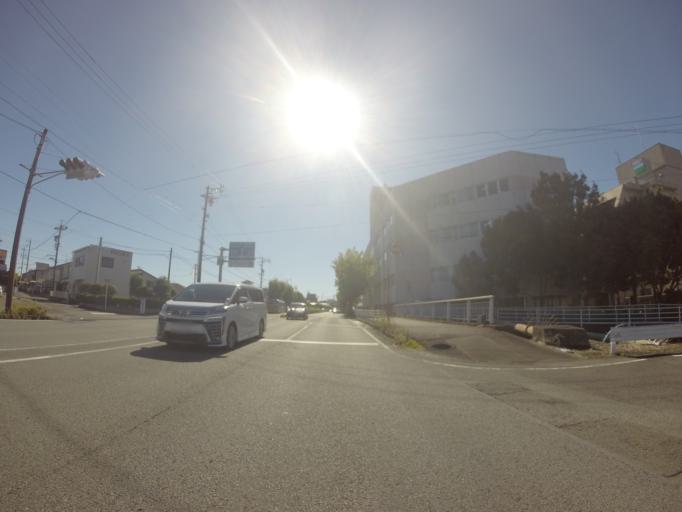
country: JP
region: Shizuoka
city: Fujieda
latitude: 34.8546
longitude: 138.2433
